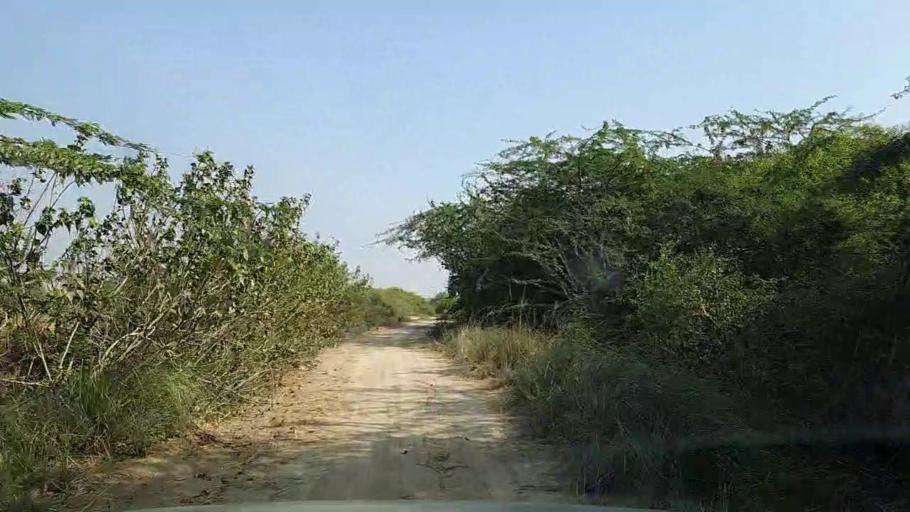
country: PK
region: Sindh
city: Mirpur Sakro
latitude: 24.5525
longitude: 67.5652
